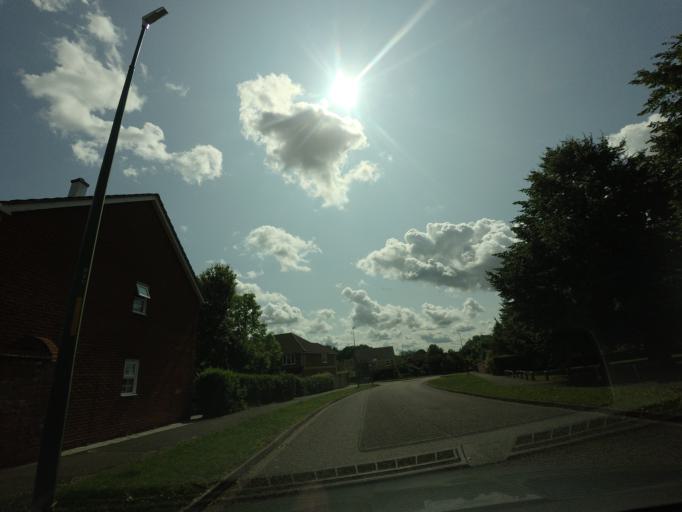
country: GB
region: England
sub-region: Kent
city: Boxley
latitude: 51.2752
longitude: 0.5606
